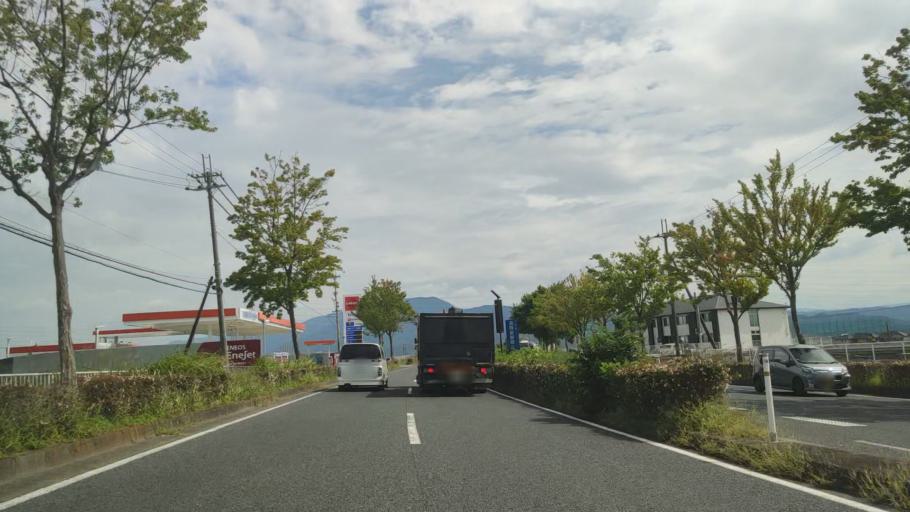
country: JP
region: Wakayama
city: Iwade
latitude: 34.2635
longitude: 135.3344
